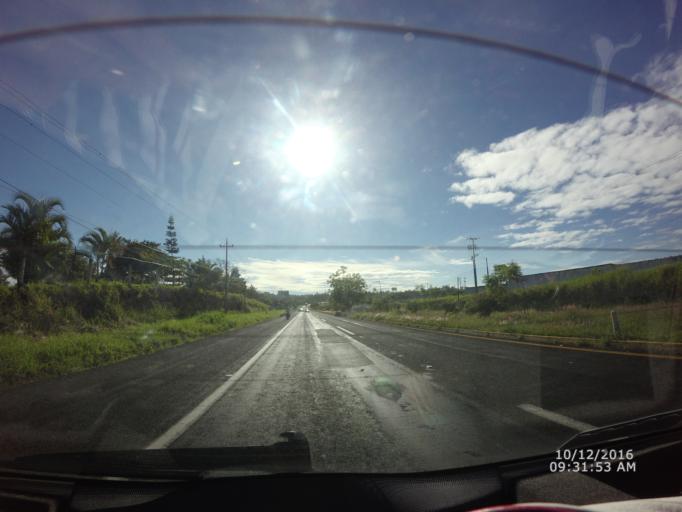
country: MX
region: Veracruz
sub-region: Emiliano Zapata
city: Jacarandas
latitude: 19.5039
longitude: -96.8481
